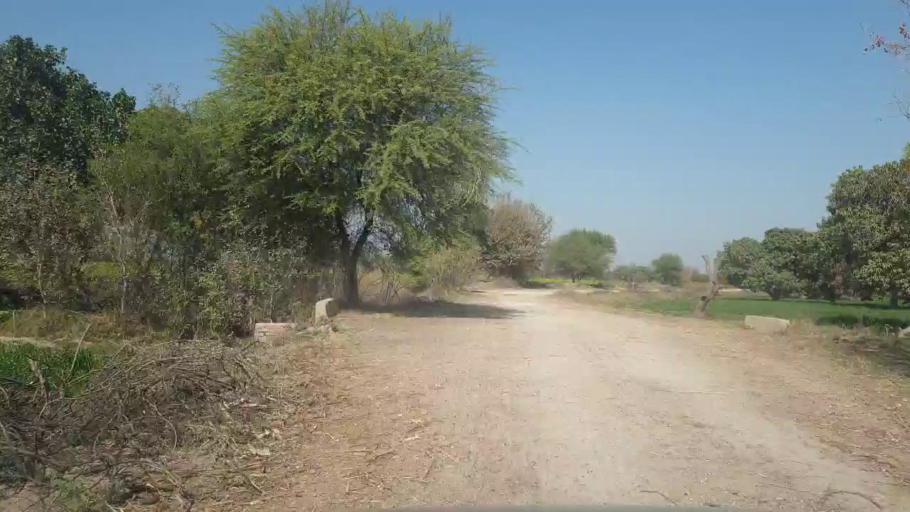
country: PK
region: Sindh
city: Chambar
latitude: 25.2999
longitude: 68.6918
